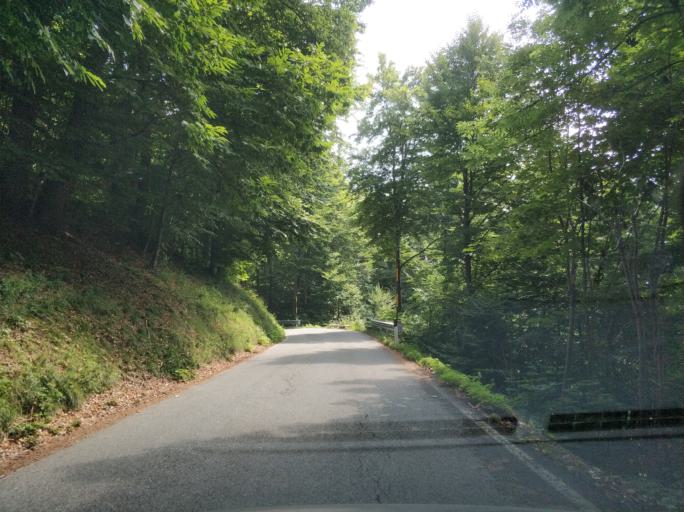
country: IT
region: Piedmont
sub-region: Provincia di Torino
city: Viu
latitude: 45.2024
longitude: 7.3717
